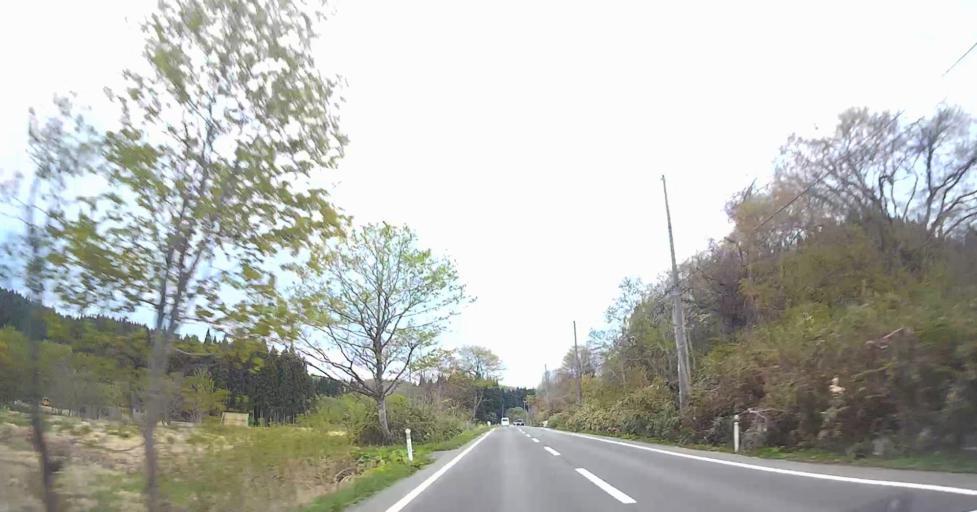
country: JP
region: Aomori
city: Goshogawara
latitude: 41.1229
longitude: 140.5214
